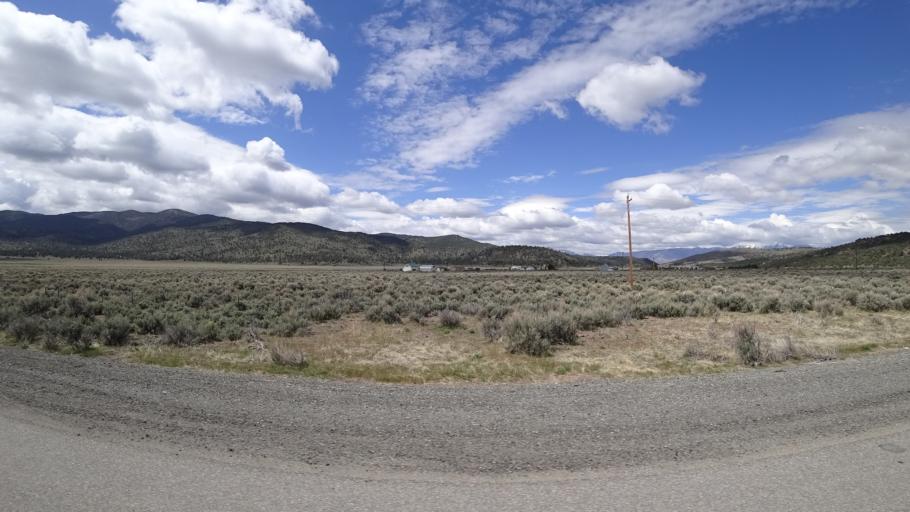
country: US
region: Nevada
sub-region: Douglas County
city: Gardnerville Ranchos
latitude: 38.7981
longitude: -119.6028
